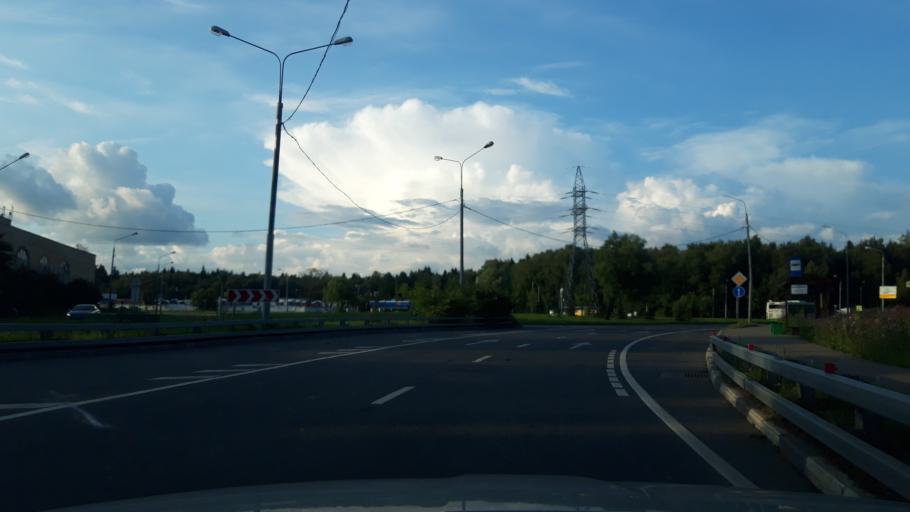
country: RU
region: Moskovskaya
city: Alabushevo
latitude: 56.0065
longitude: 37.1667
